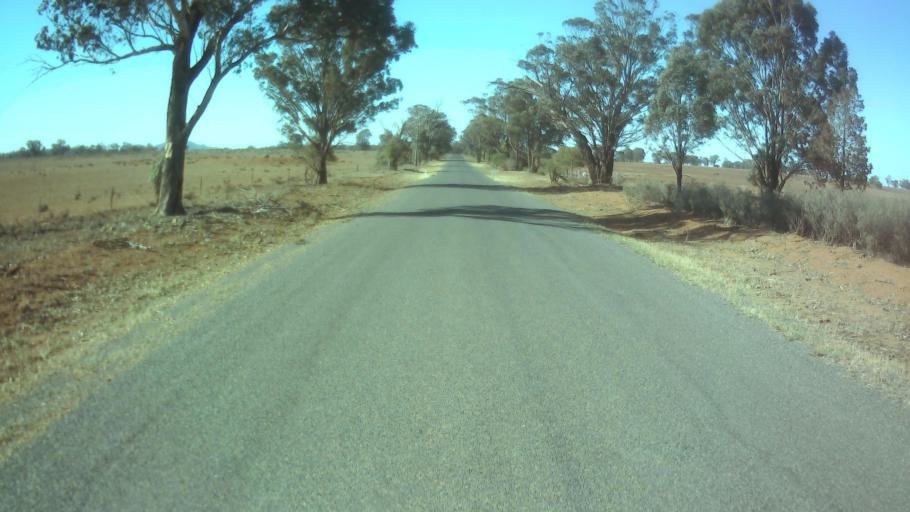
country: AU
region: New South Wales
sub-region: Forbes
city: Forbes
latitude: -33.7020
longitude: 147.8064
